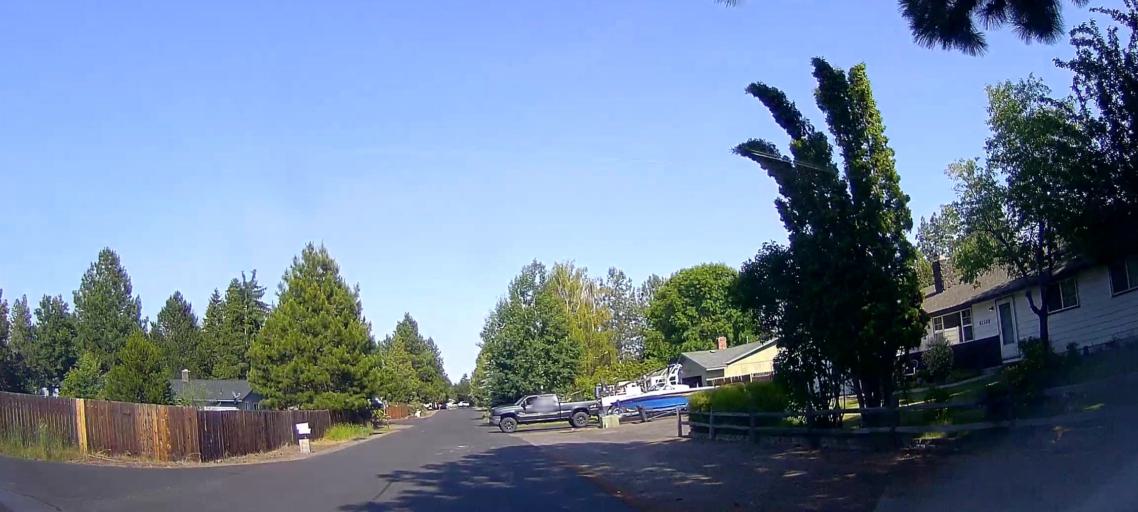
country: US
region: Oregon
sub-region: Deschutes County
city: Bend
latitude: 44.0341
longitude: -121.2829
